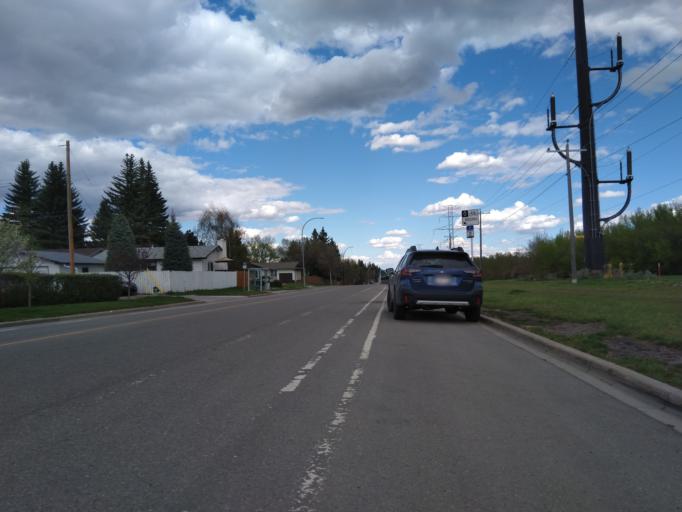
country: CA
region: Alberta
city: Calgary
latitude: 50.9945
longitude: -114.1408
